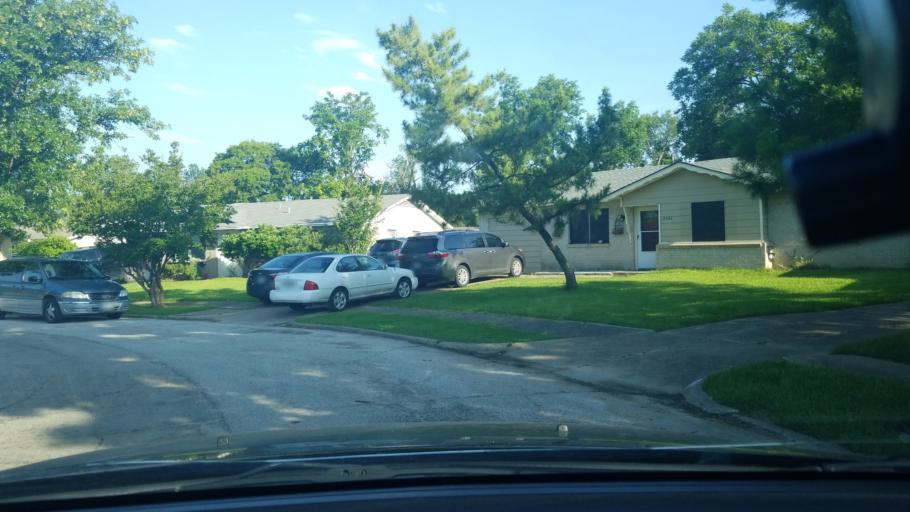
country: US
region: Texas
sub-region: Dallas County
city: Mesquite
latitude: 32.8111
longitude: -96.6381
